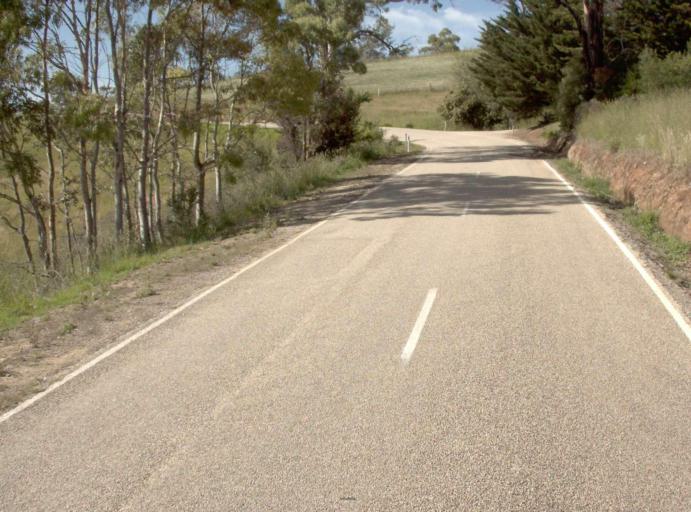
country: AU
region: Victoria
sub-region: East Gippsland
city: Lakes Entrance
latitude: -37.5085
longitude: 148.1707
